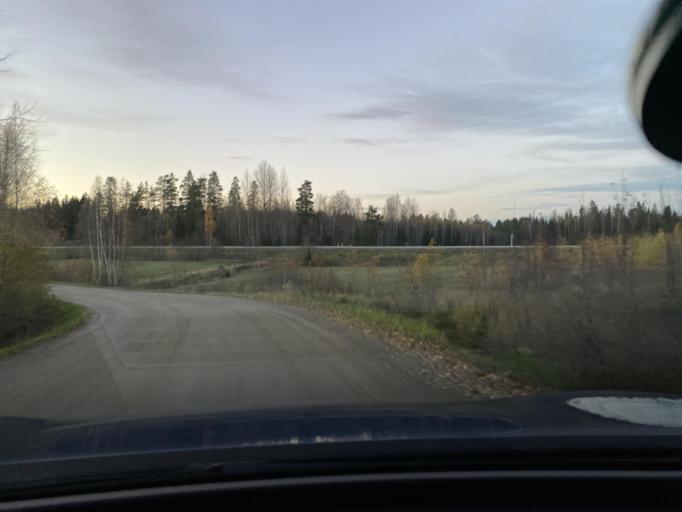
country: FI
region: Uusimaa
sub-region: Porvoo
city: Pukkila
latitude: 60.7687
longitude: 25.5235
